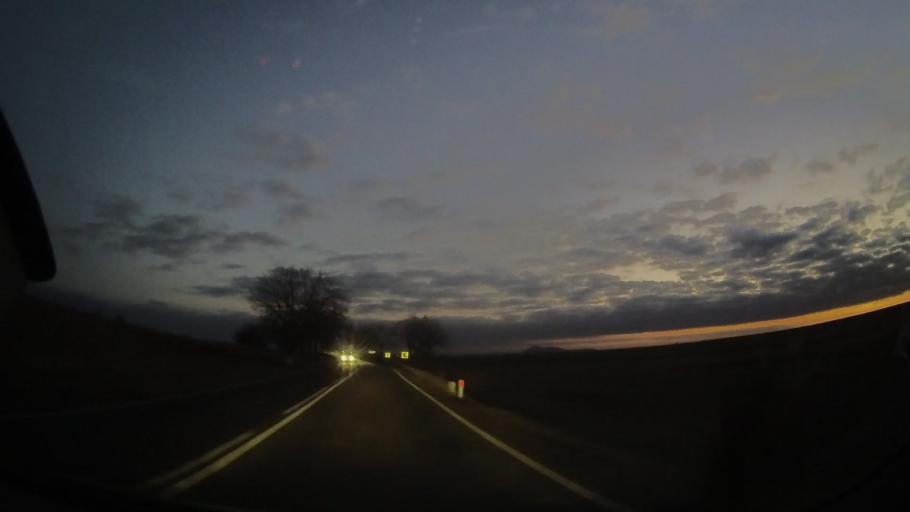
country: RO
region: Tulcea
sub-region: Comuna Frecatei
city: Cataloi
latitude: 45.0844
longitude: 28.7404
